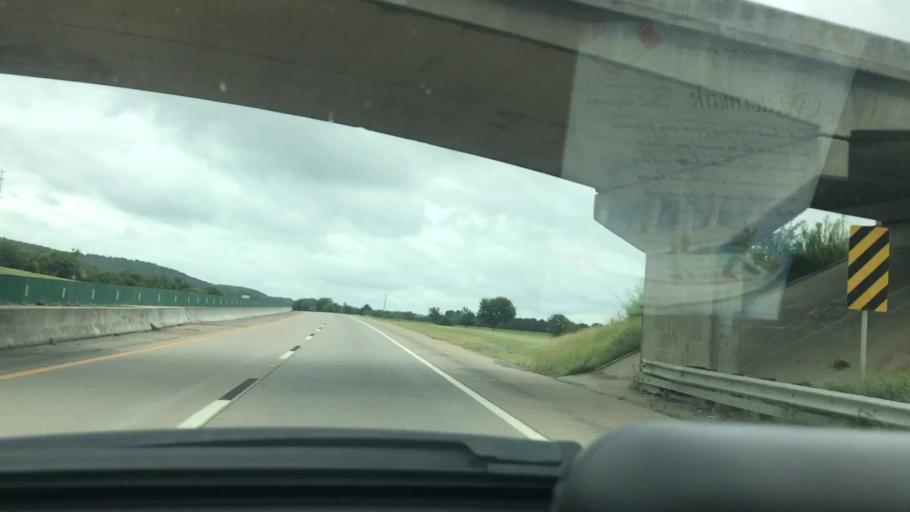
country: US
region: Oklahoma
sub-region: Pittsburg County
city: Krebs
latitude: 35.0579
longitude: -95.7067
